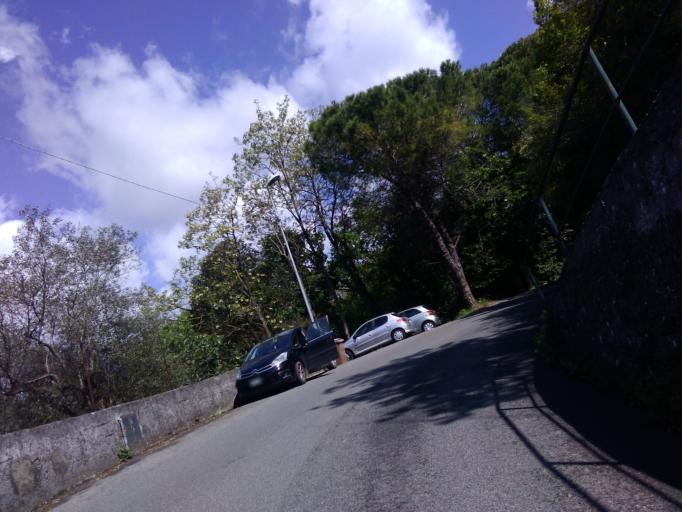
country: IT
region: Tuscany
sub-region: Provincia di Massa-Carrara
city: Carrara
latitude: 44.0801
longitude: 10.1067
